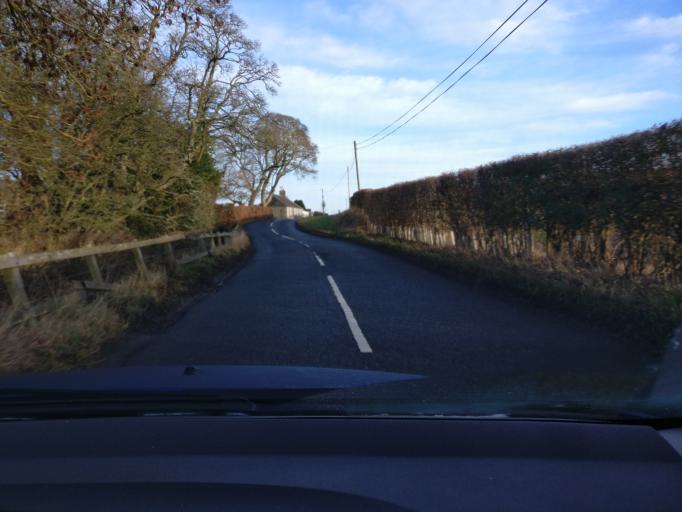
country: GB
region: Scotland
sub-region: The Scottish Borders
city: Hawick
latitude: 55.4481
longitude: -2.7637
